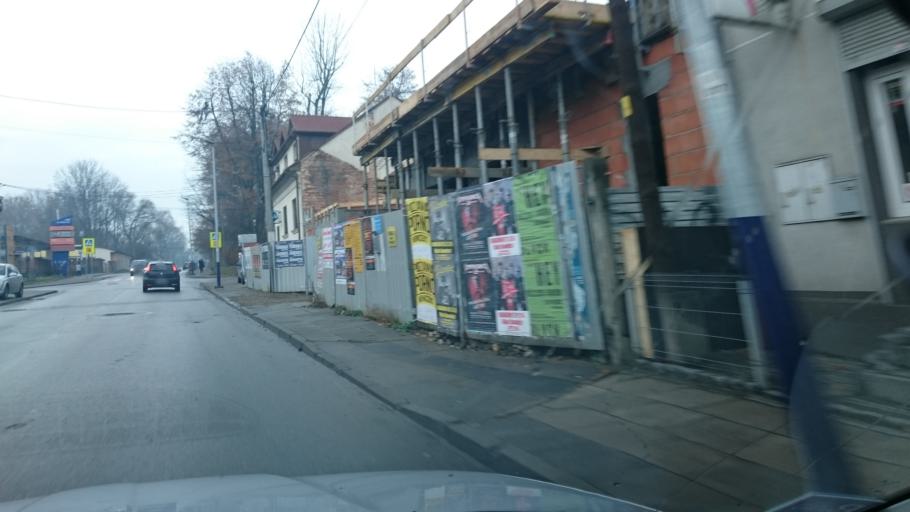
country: PL
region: Lesser Poland Voivodeship
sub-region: Krakow
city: Krakow
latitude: 50.0227
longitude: 19.9665
